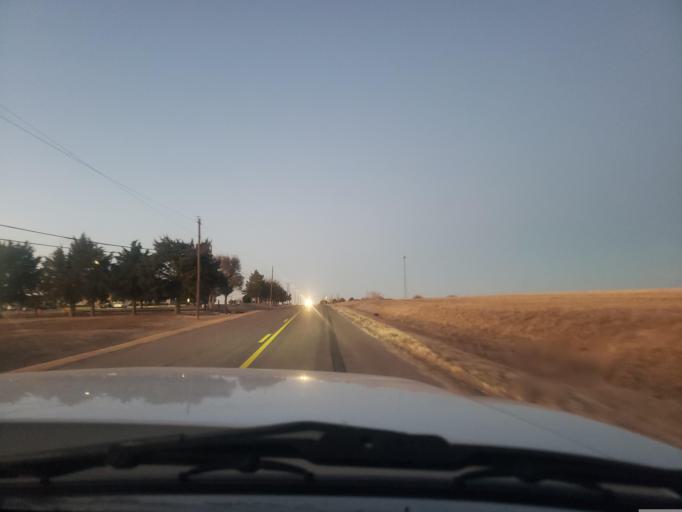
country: US
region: Kansas
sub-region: Finney County
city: Garden City
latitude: 37.9934
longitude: -100.8749
